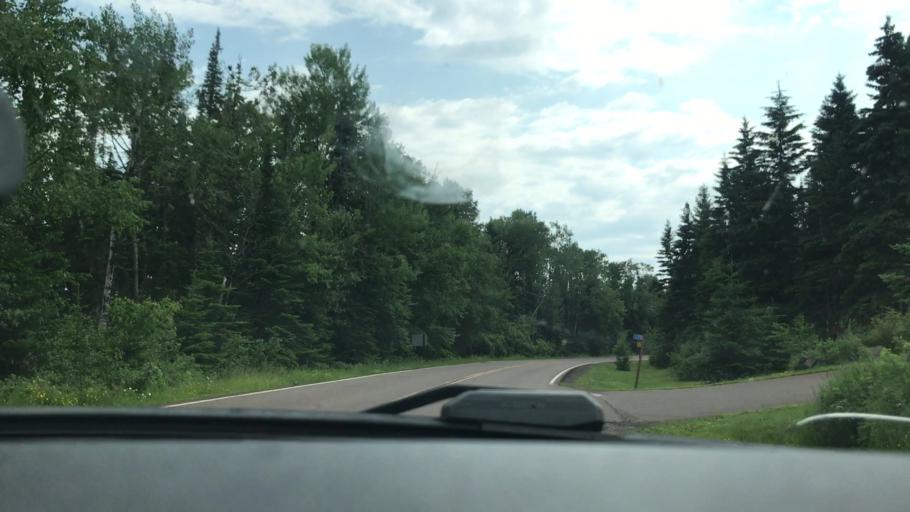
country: CA
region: Ontario
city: Neebing
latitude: 47.9604
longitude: -89.6863
